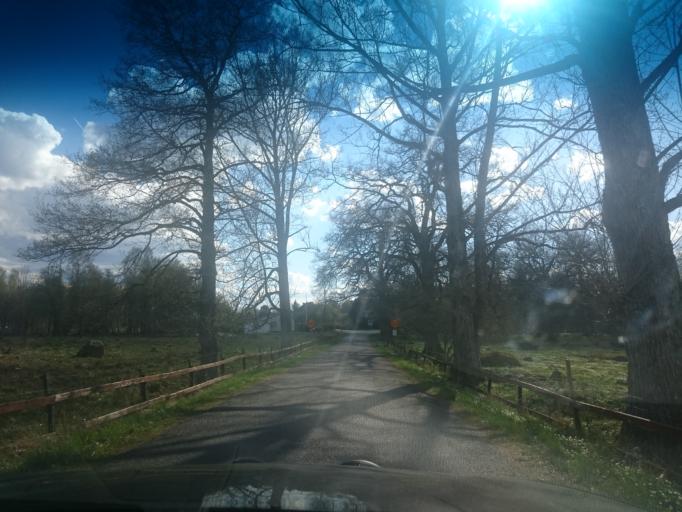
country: SE
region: Kronoberg
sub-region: Vaxjo Kommun
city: Braas
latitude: 57.1404
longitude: 15.1490
